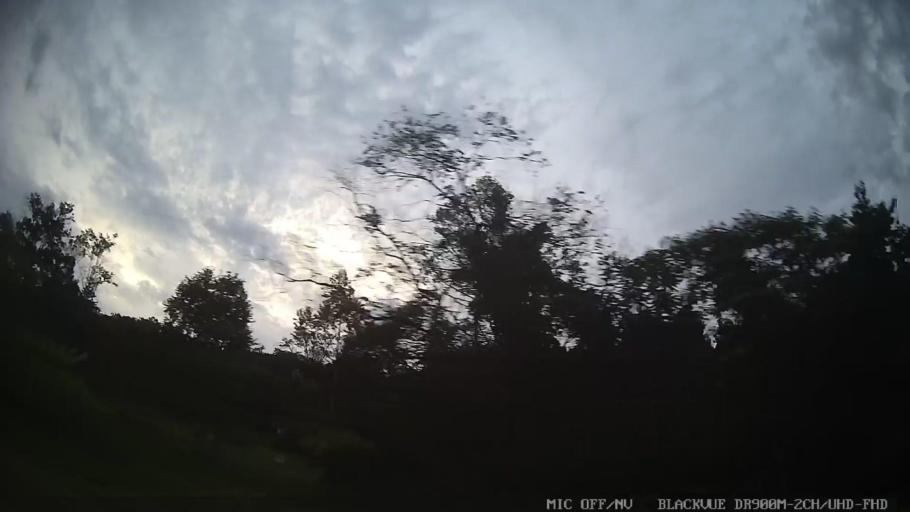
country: BR
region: Sao Paulo
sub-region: Amparo
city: Amparo
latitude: -22.8049
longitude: -46.7550
